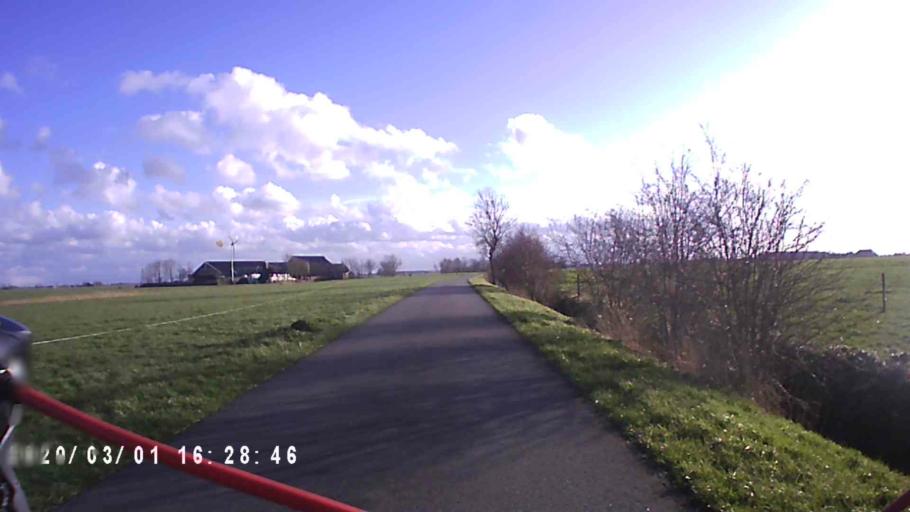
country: NL
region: Groningen
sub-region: Gemeente Zuidhorn
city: Oldehove
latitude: 53.3029
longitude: 6.4285
